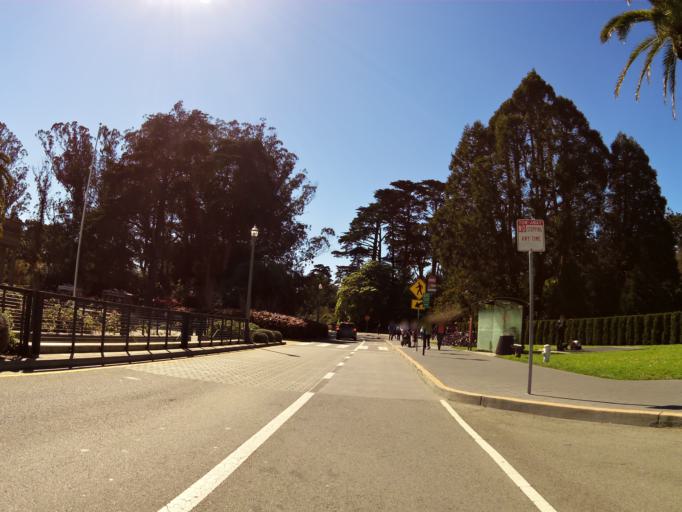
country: US
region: California
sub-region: San Francisco County
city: San Francisco
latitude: 37.7706
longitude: -122.4687
